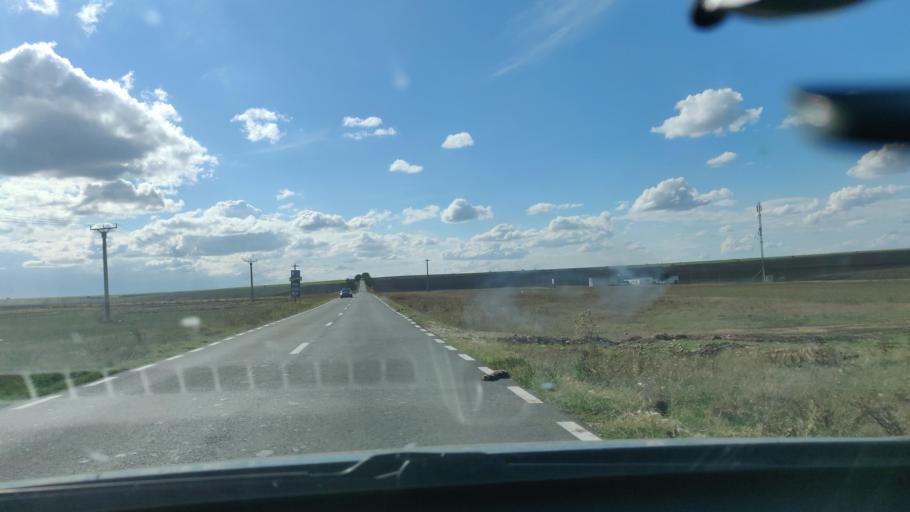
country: RO
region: Constanta
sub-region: Comuna Comana
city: Comana
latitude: 43.8235
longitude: 28.3297
